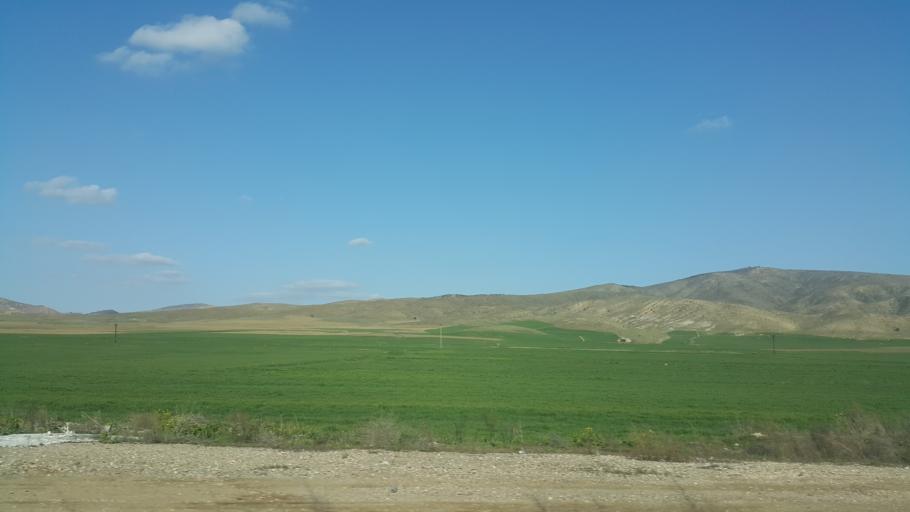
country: TR
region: Ankara
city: Sereflikochisar
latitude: 38.8456
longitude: 33.5903
